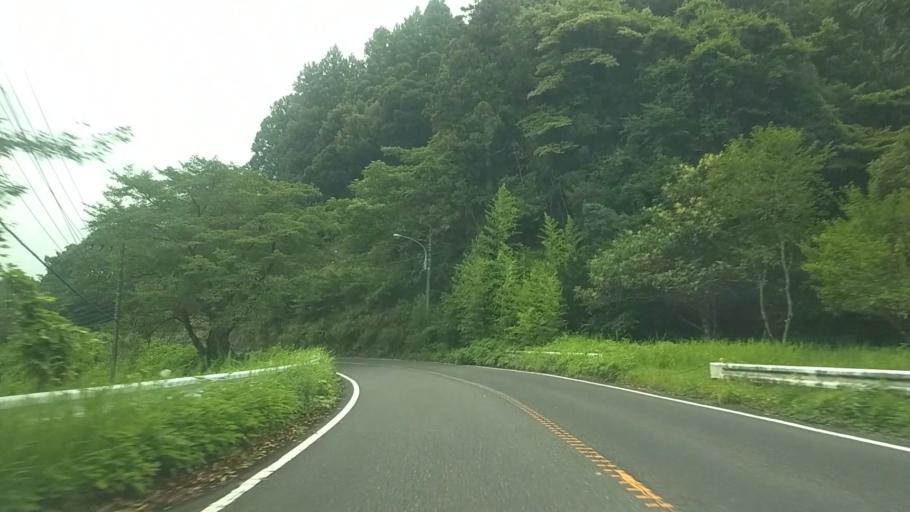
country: JP
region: Chiba
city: Kawaguchi
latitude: 35.2413
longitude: 140.0717
